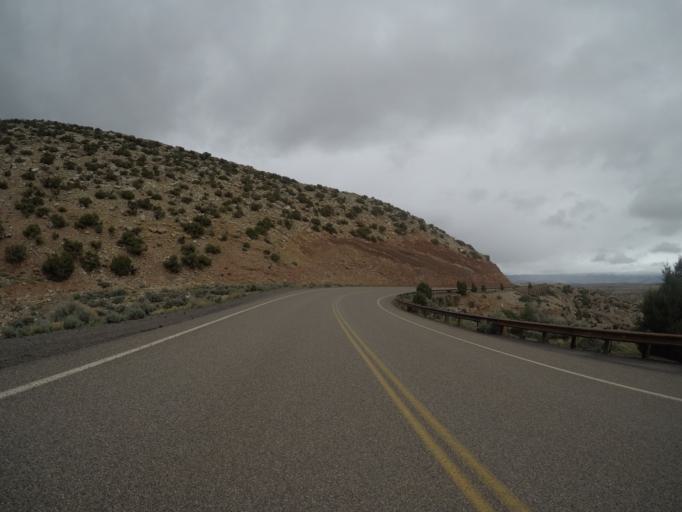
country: US
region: Wyoming
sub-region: Big Horn County
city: Lovell
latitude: 45.0414
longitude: -108.2531
